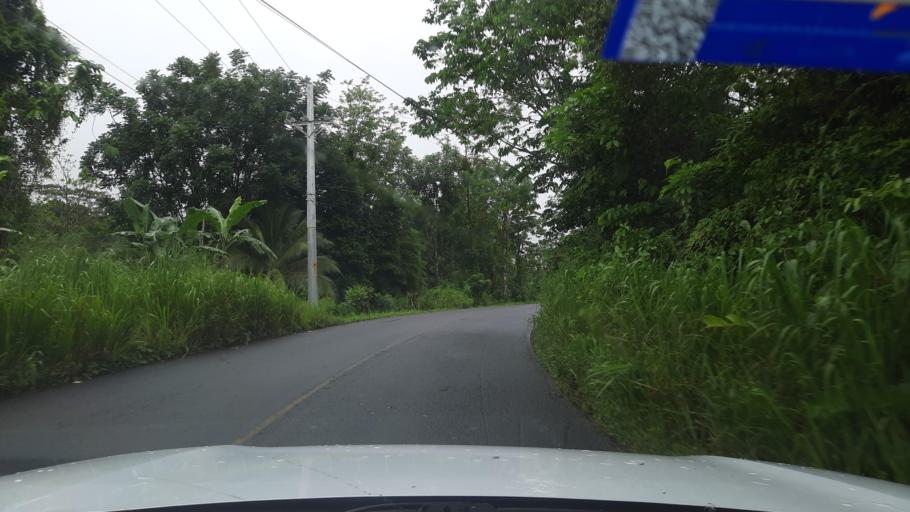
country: CR
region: Alajuela
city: Bijagua
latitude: 10.7776
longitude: -85.0279
